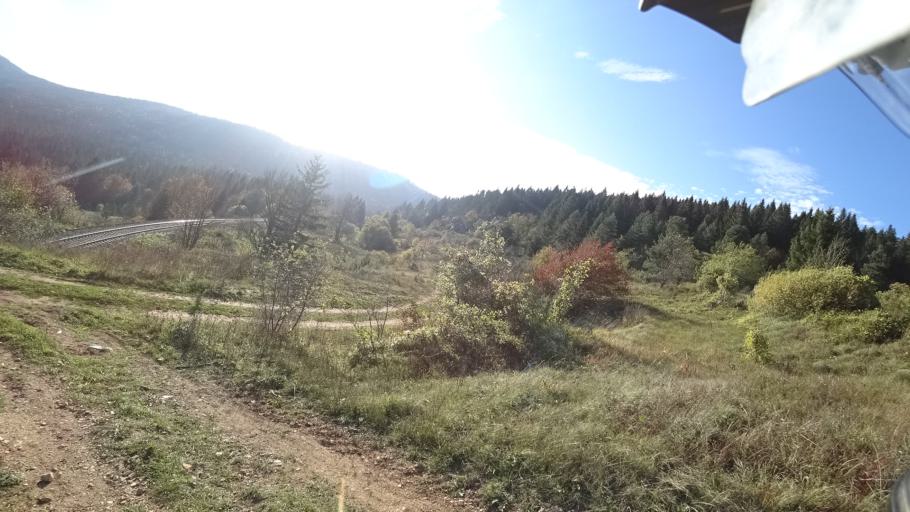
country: HR
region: Licko-Senjska
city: Jezerce
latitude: 44.9278
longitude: 15.4632
